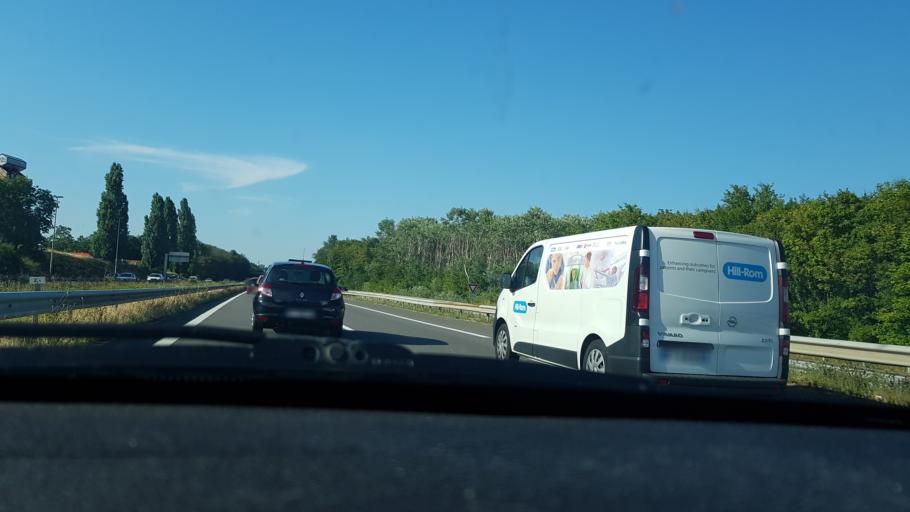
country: FR
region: Lorraine
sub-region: Departement de Meurthe-et-Moselle
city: Vandoeuvre-les-Nancy
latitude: 48.6410
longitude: 6.1813
